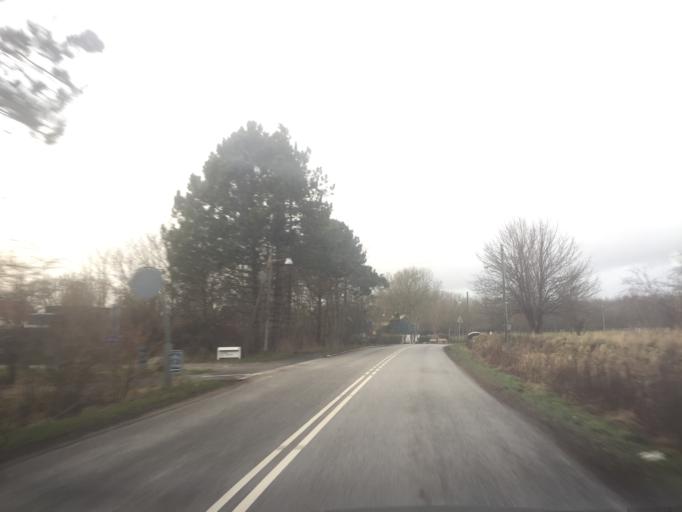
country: DK
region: Capital Region
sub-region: Albertslund Kommune
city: Albertslund
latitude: 55.6876
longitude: 12.3298
